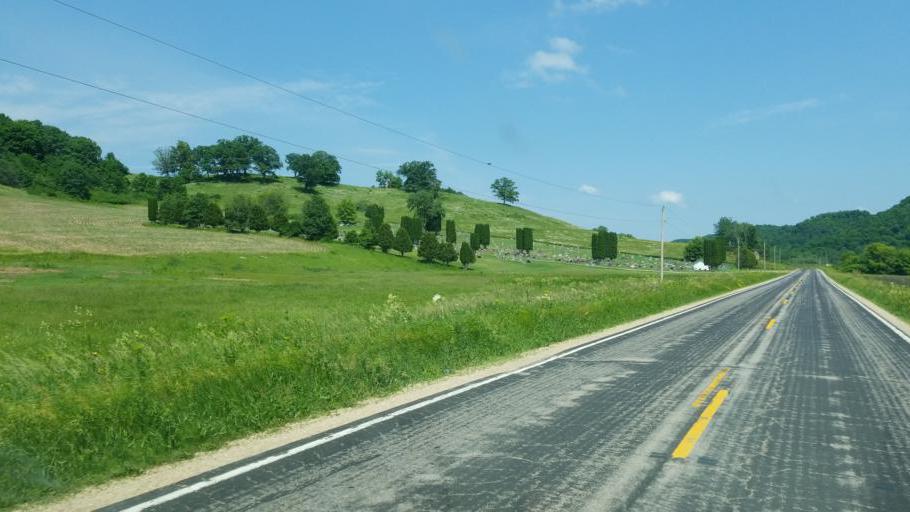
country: US
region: Wisconsin
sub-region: Monroe County
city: Cashton
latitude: 43.5742
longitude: -90.6148
